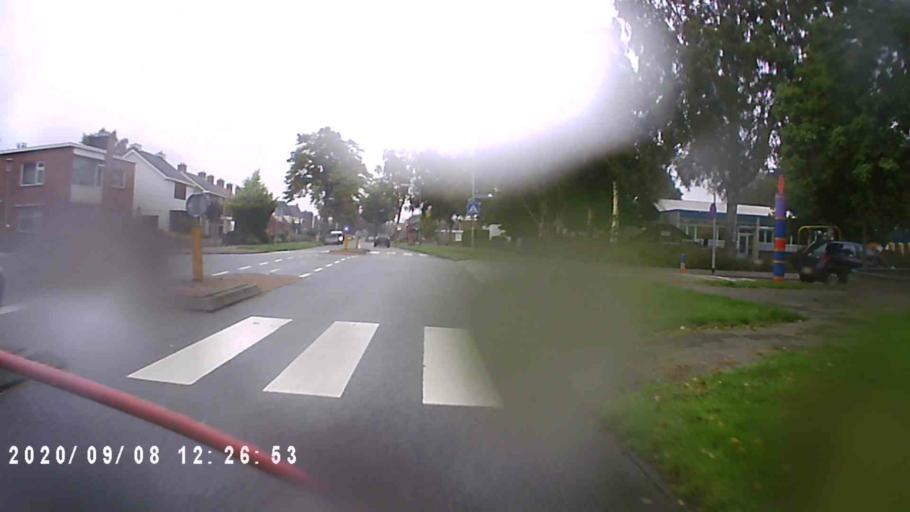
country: NL
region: Groningen
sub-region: Gemeente Veendam
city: Veendam
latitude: 53.0984
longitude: 6.8724
